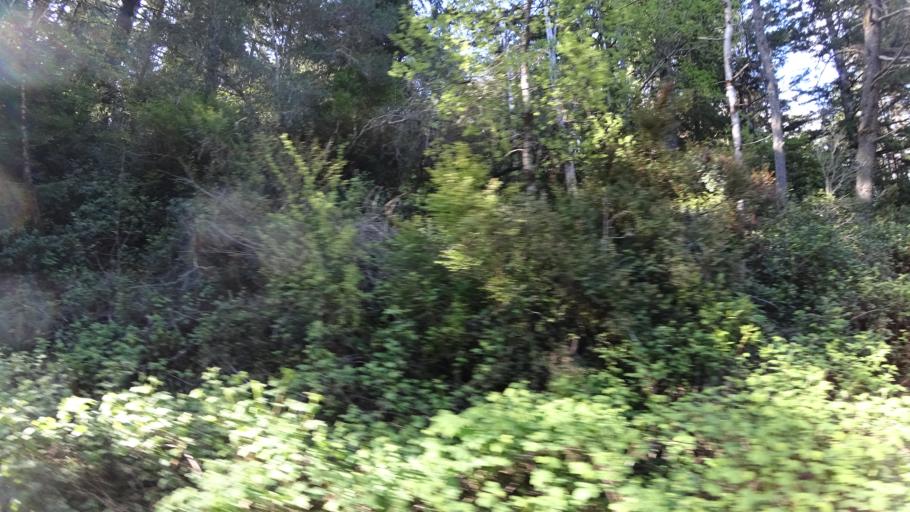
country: US
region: Oregon
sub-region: Douglas County
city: Reedsport
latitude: 43.7455
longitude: -124.1686
